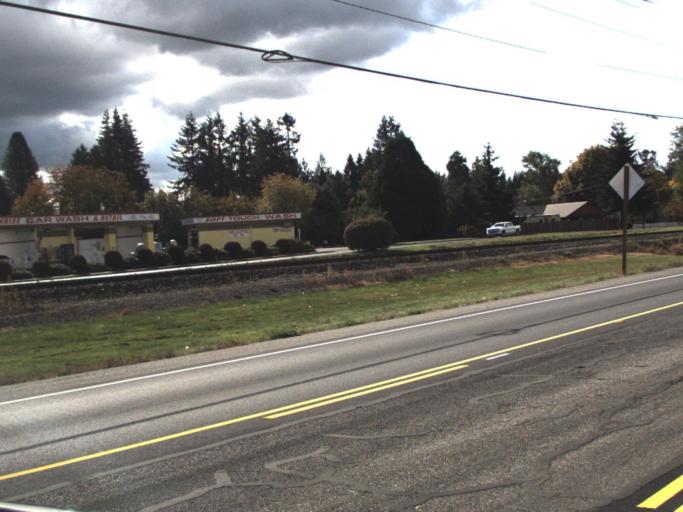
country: US
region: Washington
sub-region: Skagit County
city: Sedro-Woolley
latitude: 48.5013
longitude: -122.2569
